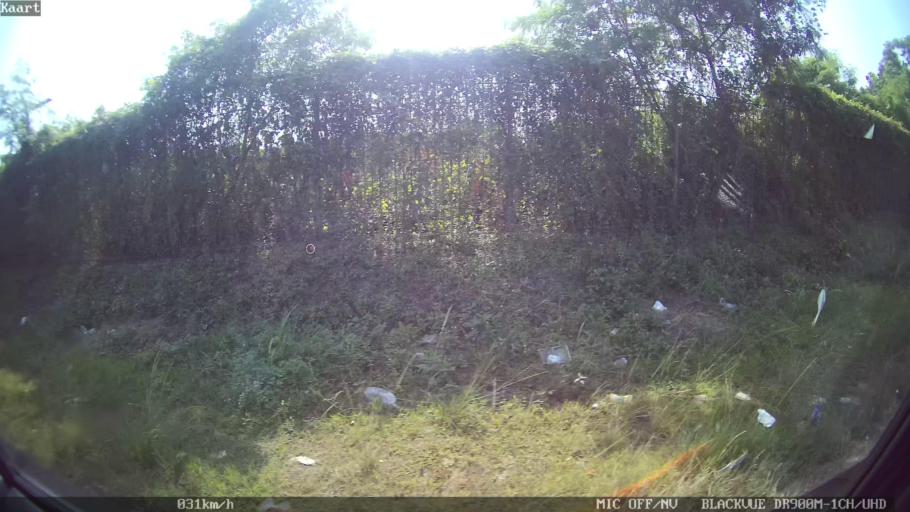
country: ID
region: Lampung
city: Natar
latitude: -5.2366
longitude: 105.1726
